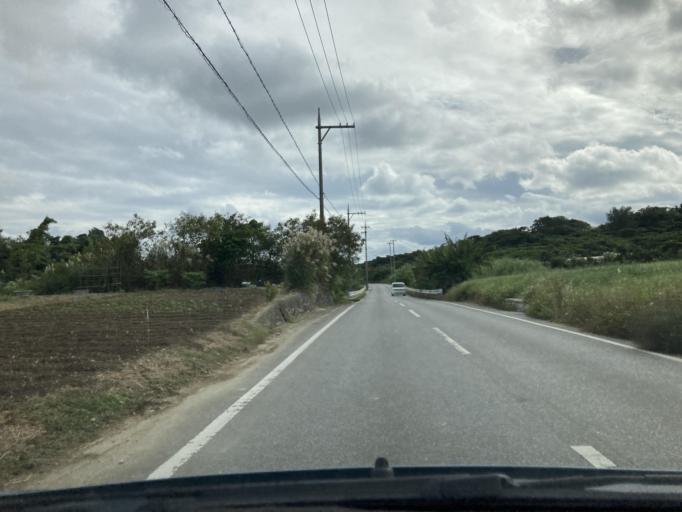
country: JP
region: Okinawa
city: Itoman
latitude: 26.1172
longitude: 127.6878
